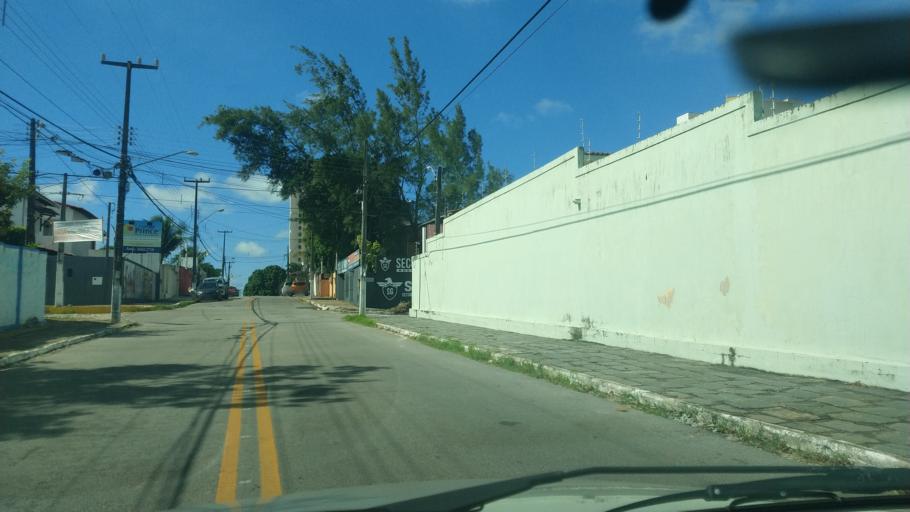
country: BR
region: Rio Grande do Norte
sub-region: Natal
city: Natal
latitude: -5.8596
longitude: -35.2008
